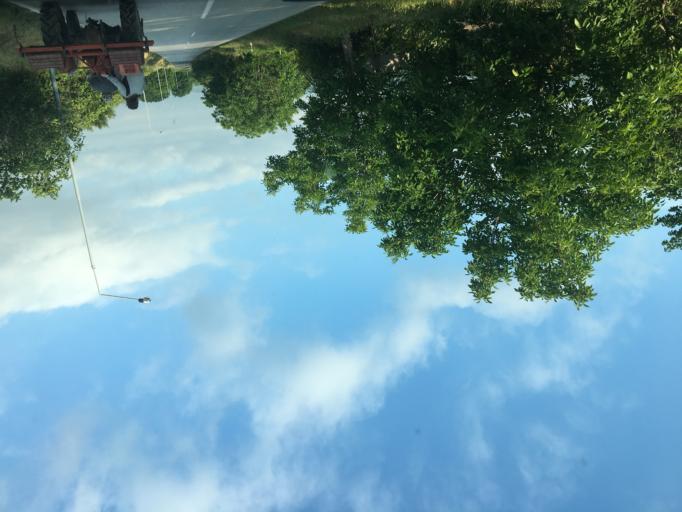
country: MK
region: Valandovo
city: Valandovo
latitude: 41.3129
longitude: 22.5535
